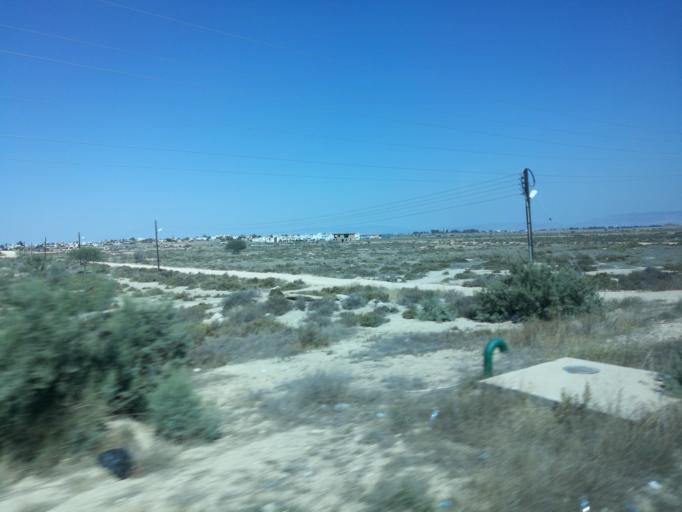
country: CY
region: Ammochostos
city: Famagusta
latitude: 35.1621
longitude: 33.8994
